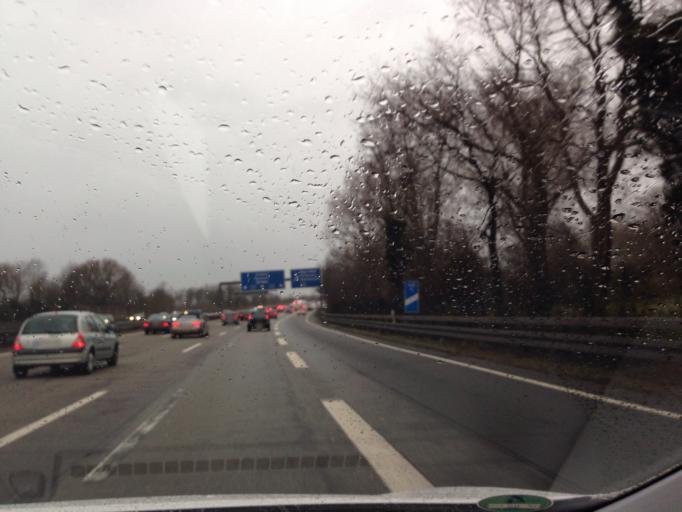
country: DE
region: North Rhine-Westphalia
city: Meiderich
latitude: 51.4824
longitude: 6.8133
